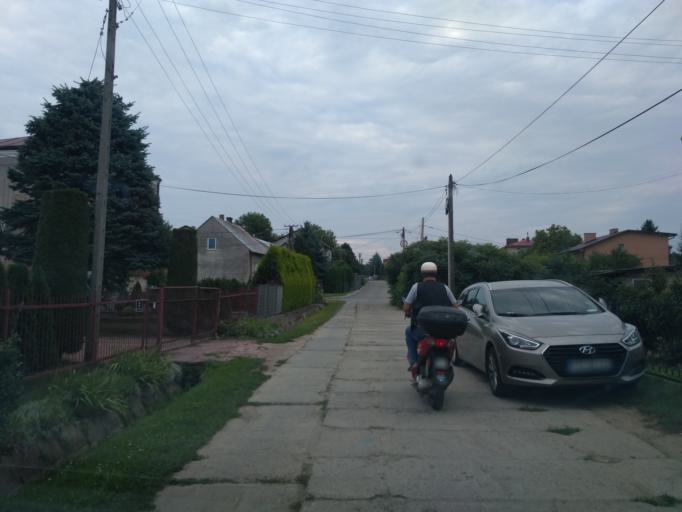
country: PL
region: Subcarpathian Voivodeship
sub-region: Powiat sanocki
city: Sanok
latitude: 49.5696
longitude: 22.1688
